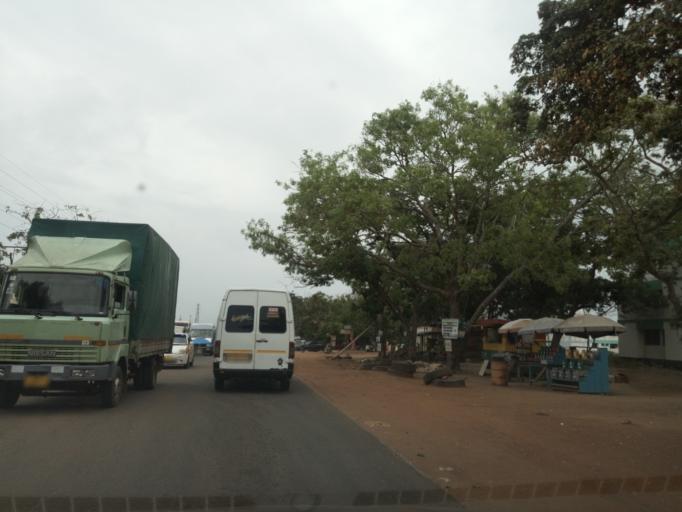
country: GH
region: Greater Accra
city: Tema
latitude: 5.6218
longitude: -0.0220
